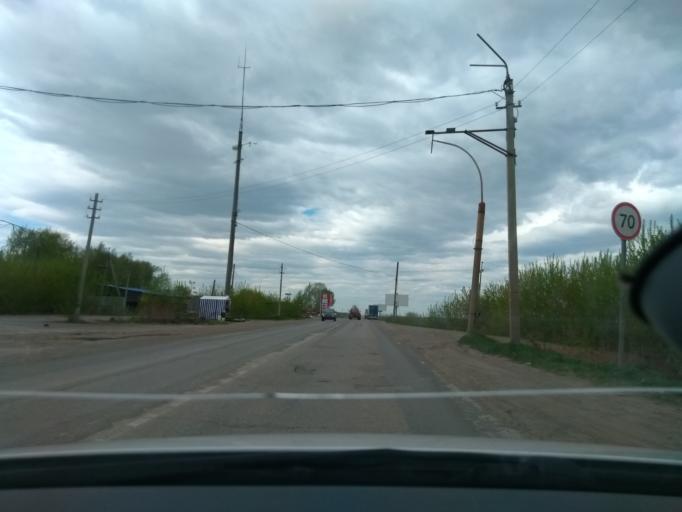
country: RU
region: Perm
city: Lobanovo
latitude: 57.8644
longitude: 56.2938
